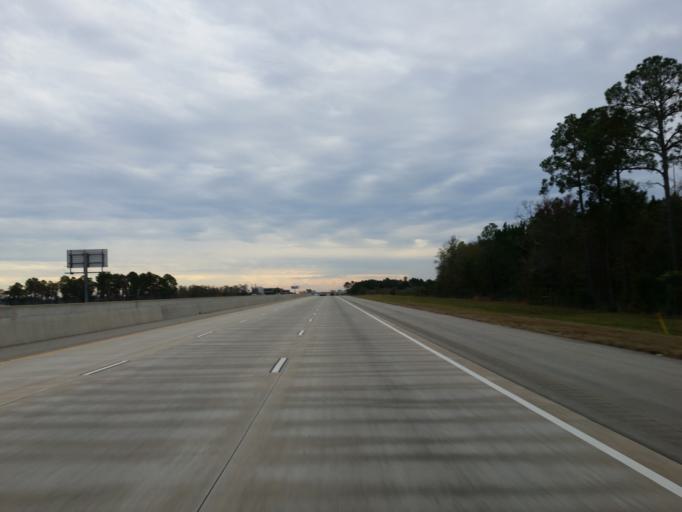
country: US
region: Georgia
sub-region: Cook County
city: Sparks
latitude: 31.1983
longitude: -83.4569
